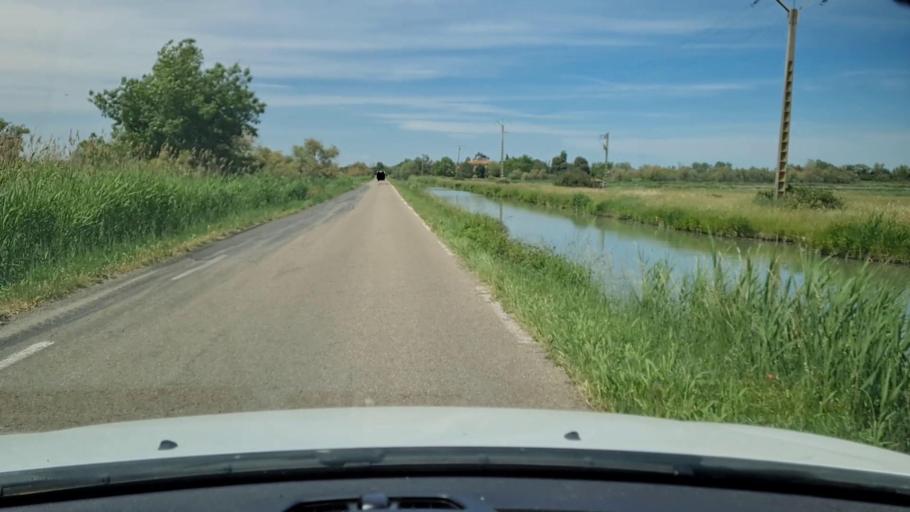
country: FR
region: Languedoc-Roussillon
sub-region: Departement du Gard
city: Vauvert
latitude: 43.6006
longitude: 4.3390
